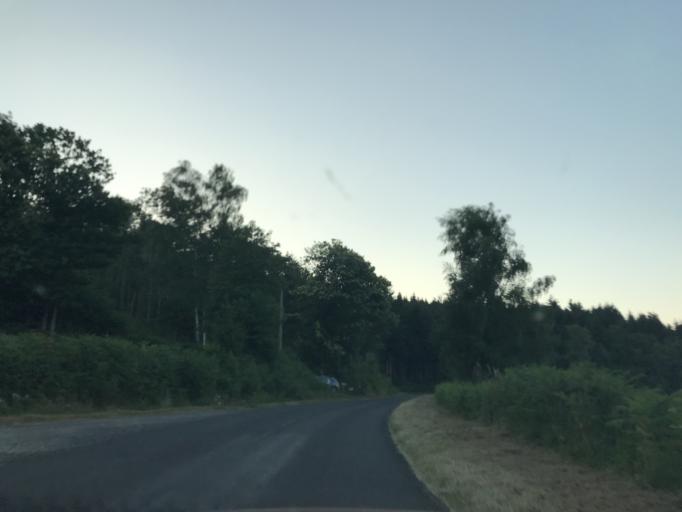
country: FR
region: Auvergne
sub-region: Departement du Puy-de-Dome
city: Celles-sur-Durolle
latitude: 45.7496
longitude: 3.6562
